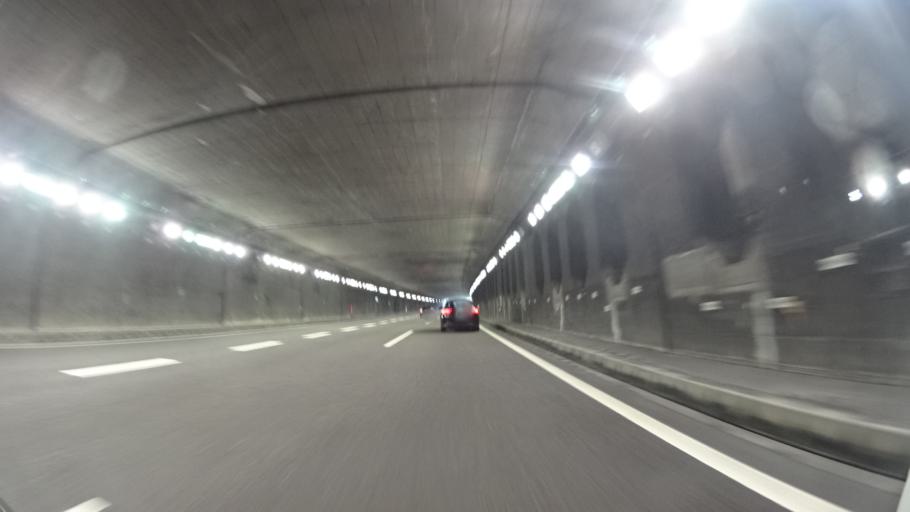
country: JP
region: Ehime
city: Niihama
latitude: 33.9313
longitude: 133.3515
